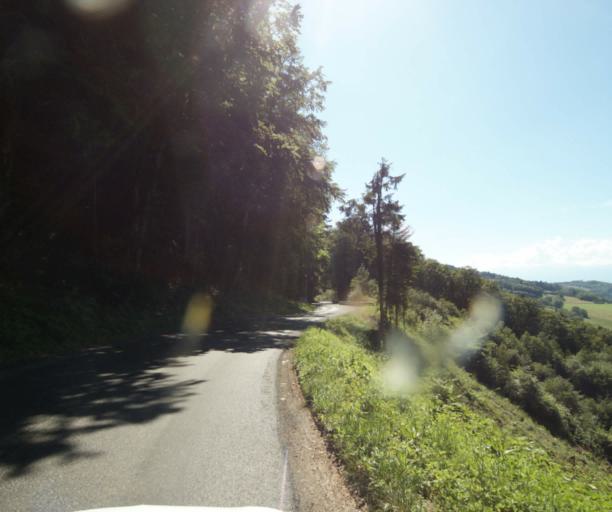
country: FR
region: Rhone-Alpes
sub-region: Departement de la Haute-Savoie
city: Bons-en-Chablais
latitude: 46.2496
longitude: 6.3845
